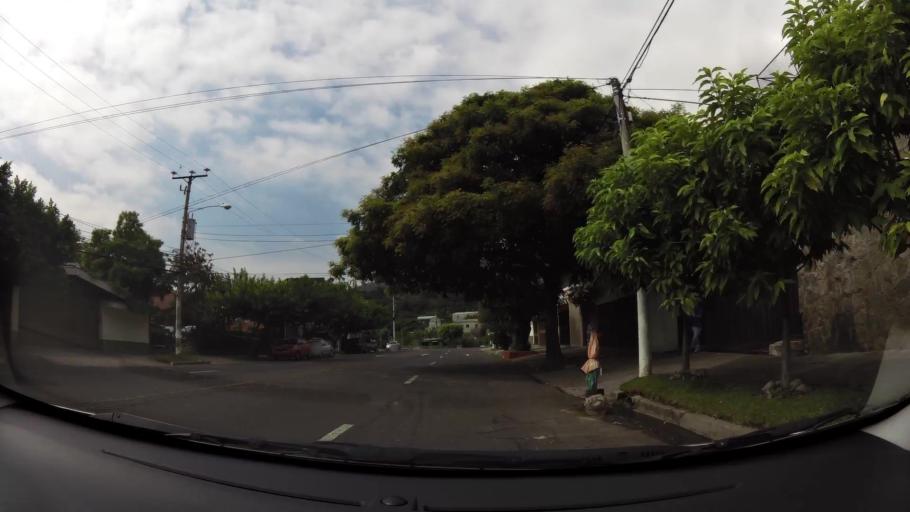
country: SV
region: La Libertad
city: Santa Tecla
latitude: 13.7045
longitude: -89.2585
